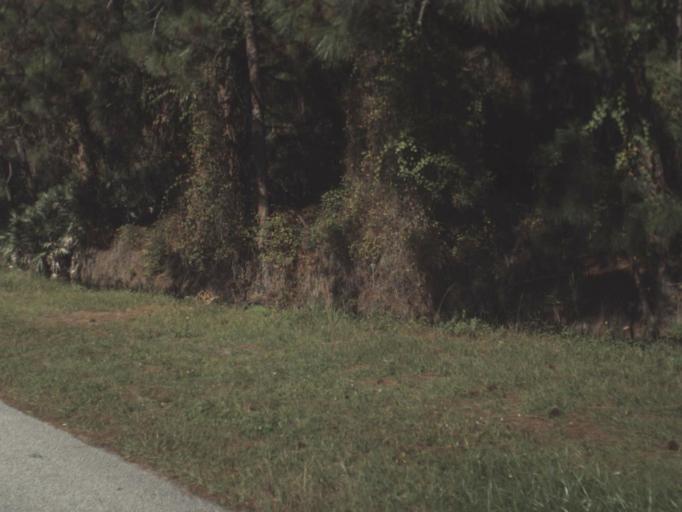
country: US
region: Florida
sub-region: Brevard County
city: Rockledge
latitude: 28.2941
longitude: -80.7141
